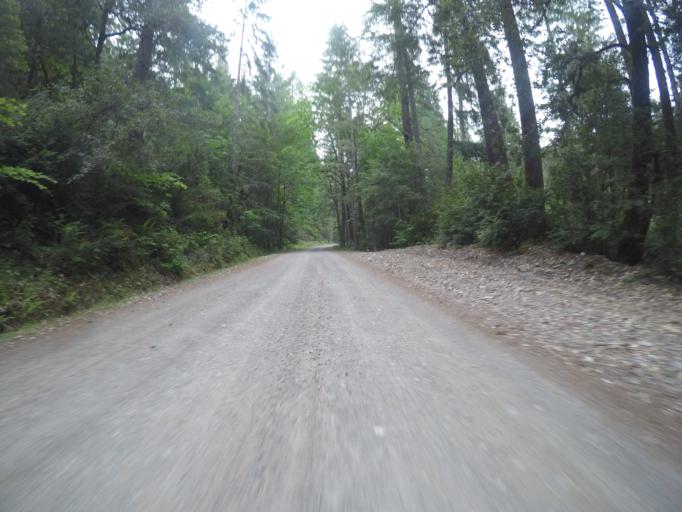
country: US
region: California
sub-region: Del Norte County
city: Bertsch-Oceanview
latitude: 41.7244
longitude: -123.8951
